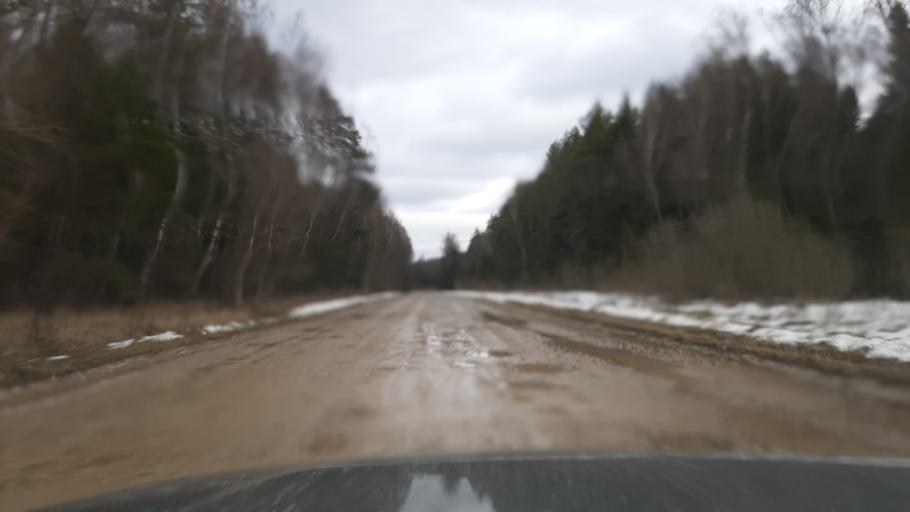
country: RU
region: Ivanovo
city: Teykovo
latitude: 56.8843
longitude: 40.6399
